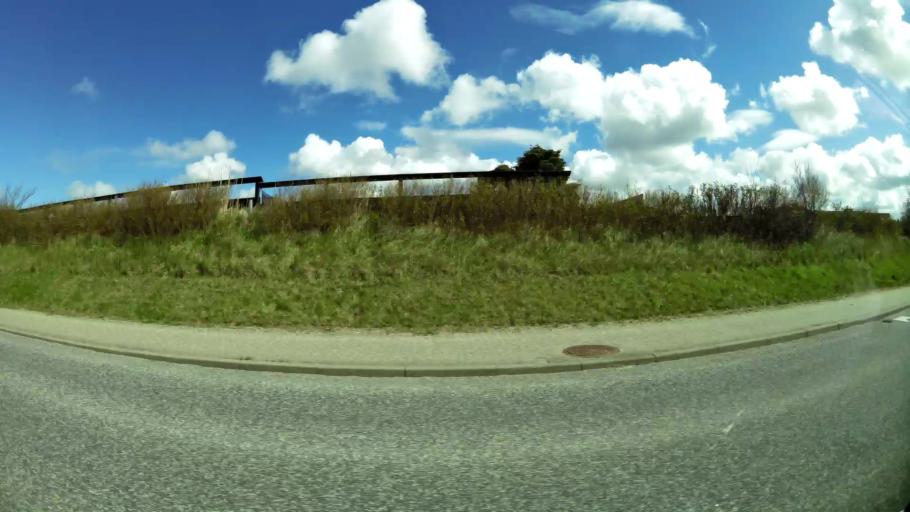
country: DK
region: North Denmark
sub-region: Hjorring Kommune
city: Hirtshals
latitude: 57.5305
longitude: 9.9473
